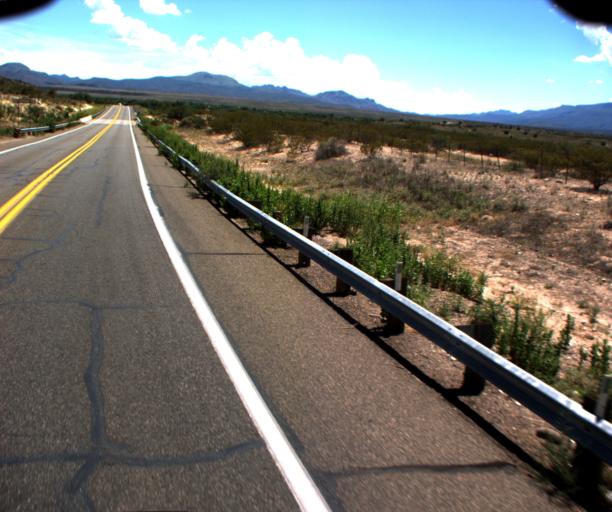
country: US
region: Arizona
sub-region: Yavapai County
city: Camp Verde
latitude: 34.5332
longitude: -111.8121
